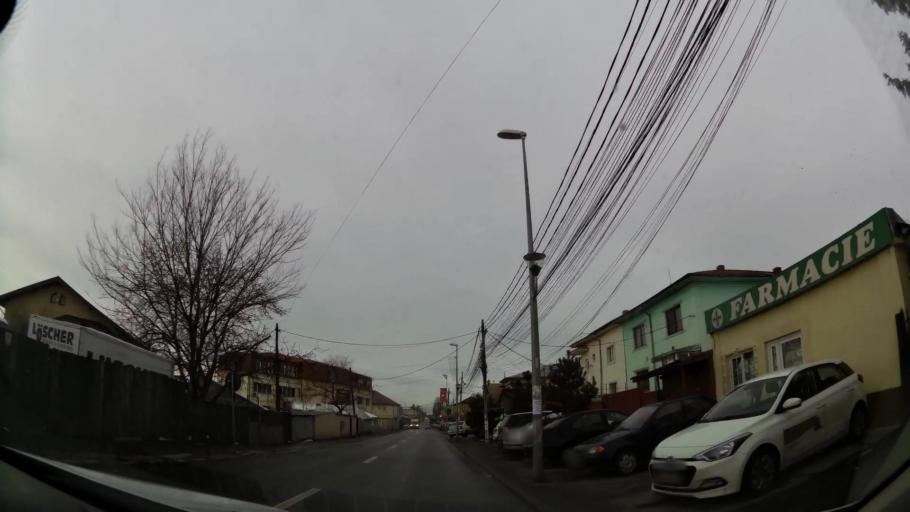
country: RO
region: Ilfov
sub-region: Comuna Pantelimon
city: Pantelimon
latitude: 44.4512
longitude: 26.2068
